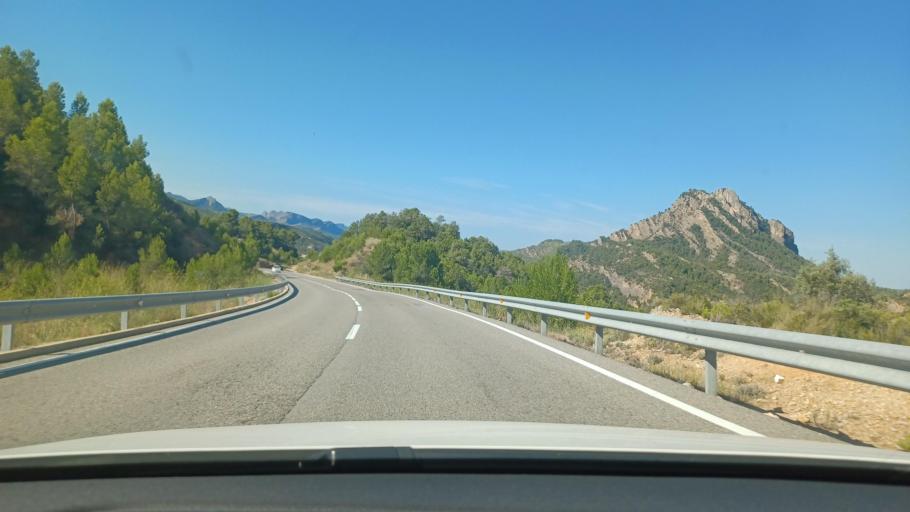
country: ES
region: Catalonia
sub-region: Provincia de Tarragona
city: Bot
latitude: 40.9654
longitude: 0.3667
